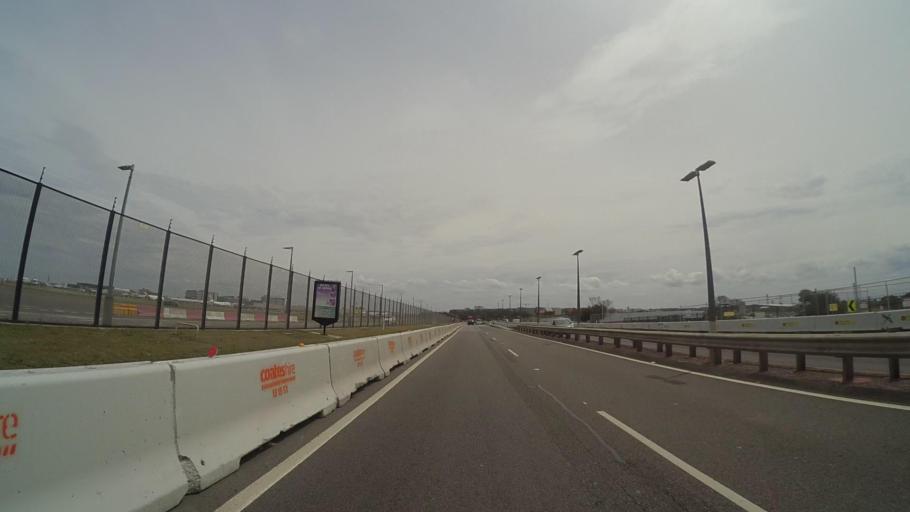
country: AU
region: New South Wales
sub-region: Botany Bay
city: Mascot
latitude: -33.9266
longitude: 151.1739
